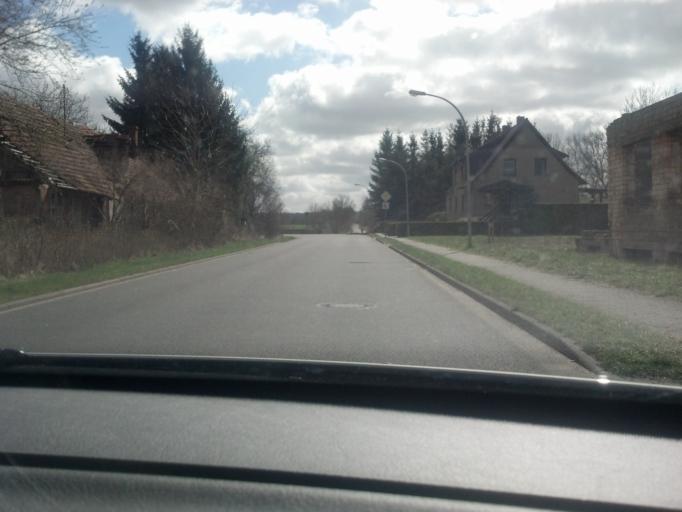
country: DE
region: Brandenburg
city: Gerdshagen
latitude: 53.2928
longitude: 12.1753
